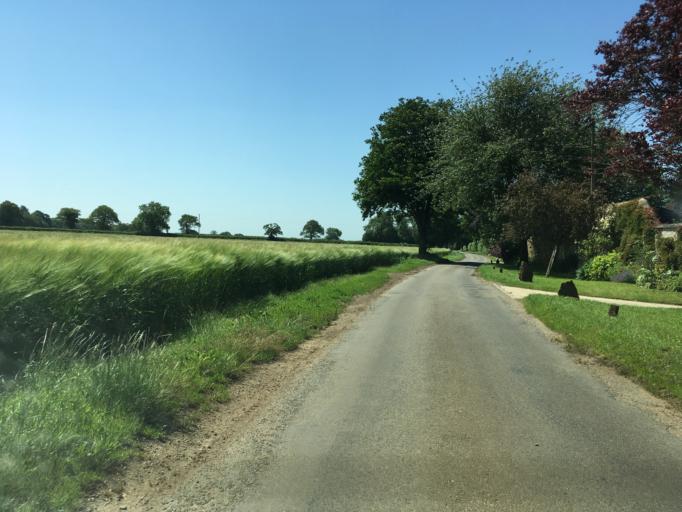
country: GB
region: England
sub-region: Northamptonshire
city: Brackley
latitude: 51.9959
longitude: -1.1061
